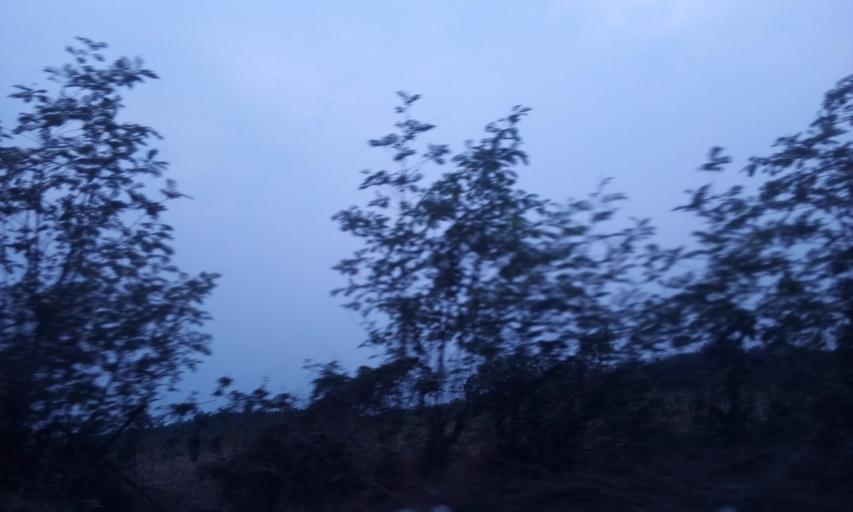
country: TH
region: Chon Buri
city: Ko Chan
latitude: 13.4903
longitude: 101.2755
